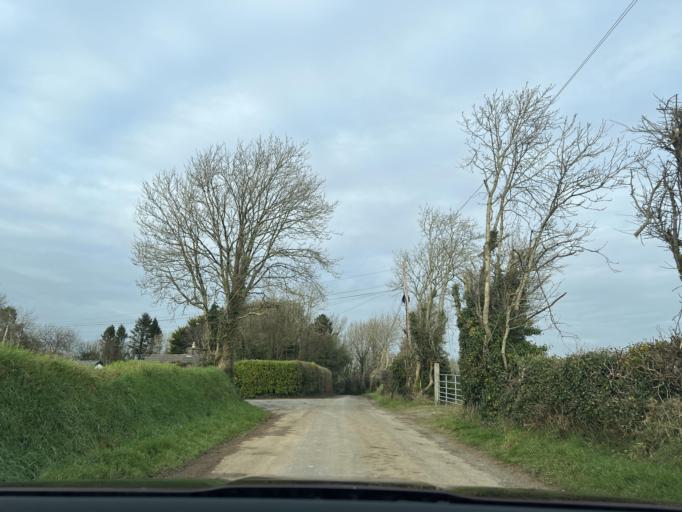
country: IE
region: Leinster
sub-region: Loch Garman
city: Loch Garman
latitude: 52.3646
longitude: -6.5305
